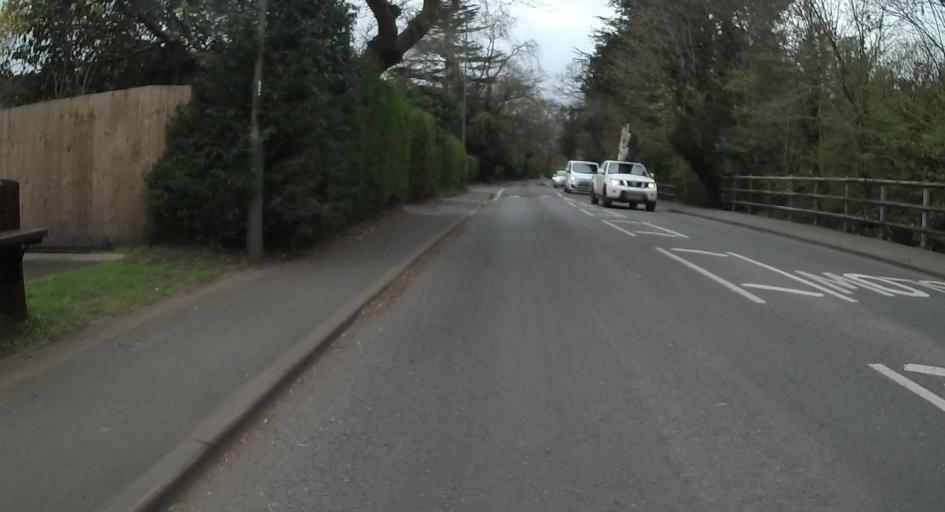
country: GB
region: England
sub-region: Surrey
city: West Byfleet
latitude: 51.3444
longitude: -0.5129
